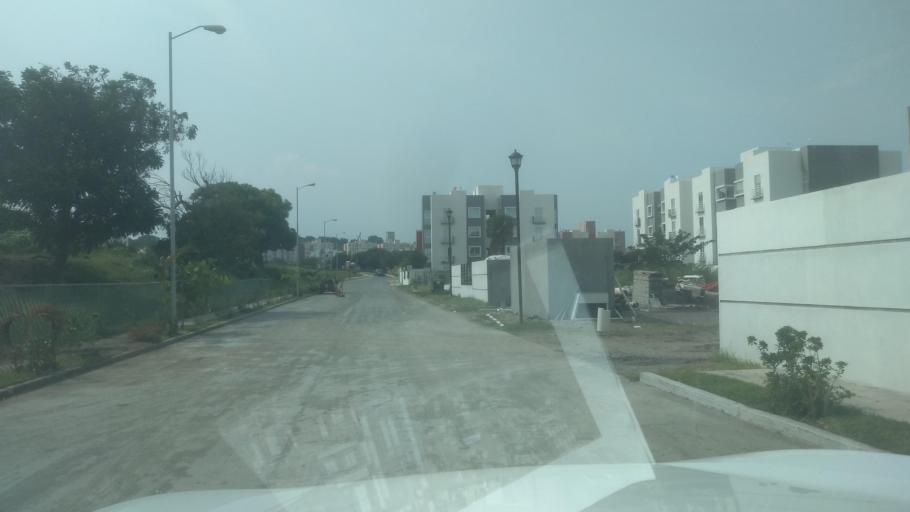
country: MX
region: Veracruz
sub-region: Veracruz
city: Lomas de Rio Medio Cuatro
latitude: 19.1772
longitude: -96.2078
